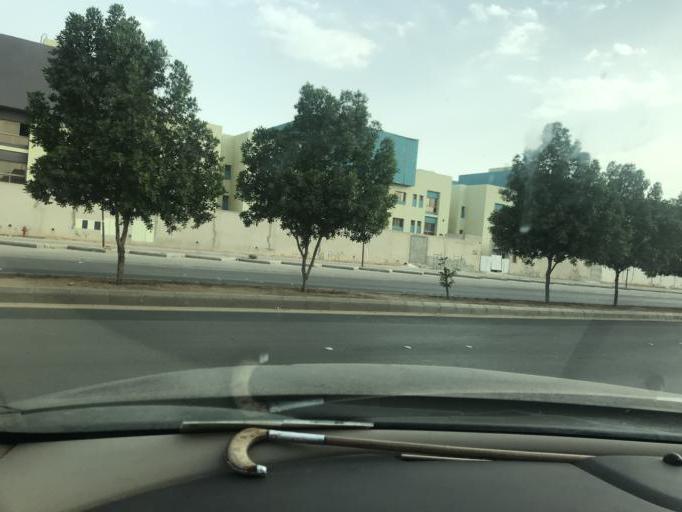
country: SA
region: Ar Riyad
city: Riyadh
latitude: 24.7799
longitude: 46.7134
